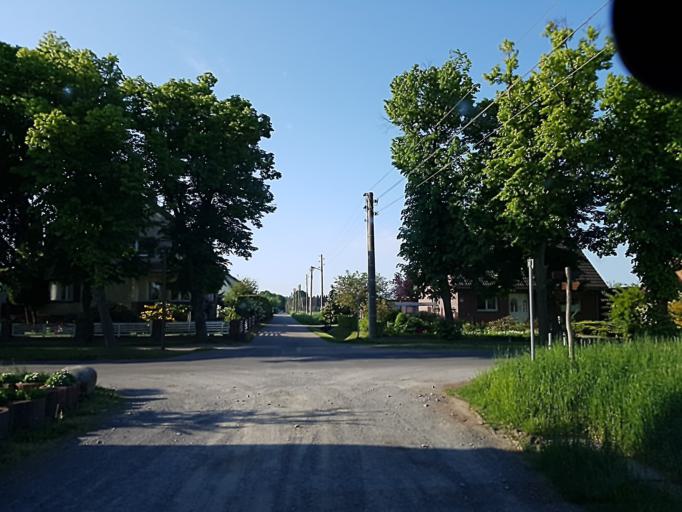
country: DE
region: Brandenburg
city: Doberlug-Kirchhain
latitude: 51.6380
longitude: 13.5519
